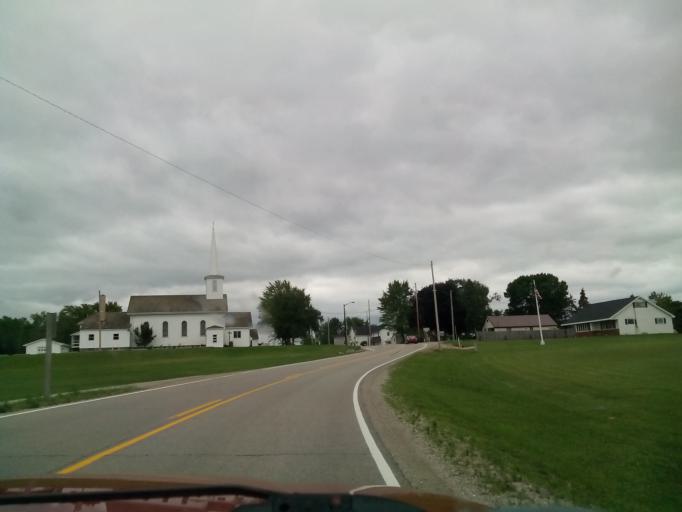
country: US
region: Wisconsin
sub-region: Outagamie County
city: Hortonville
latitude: 44.3751
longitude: -88.5840
